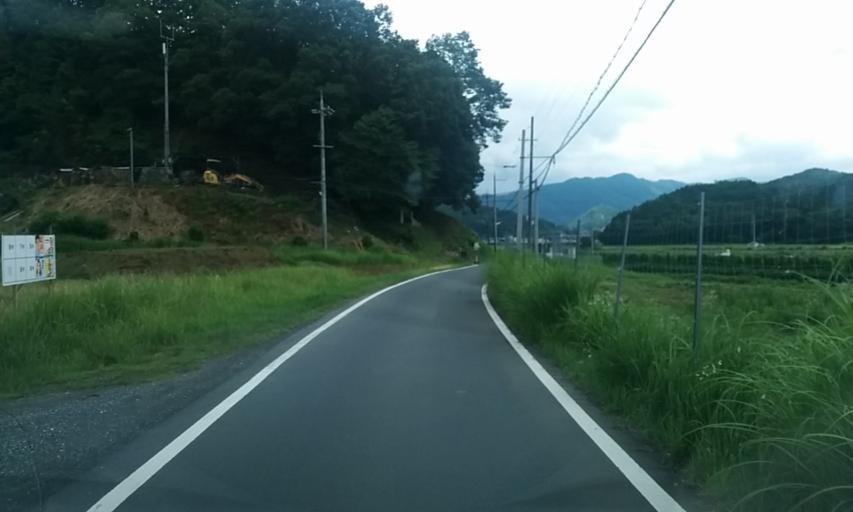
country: JP
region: Kyoto
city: Kameoka
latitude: 35.0869
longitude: 135.4915
